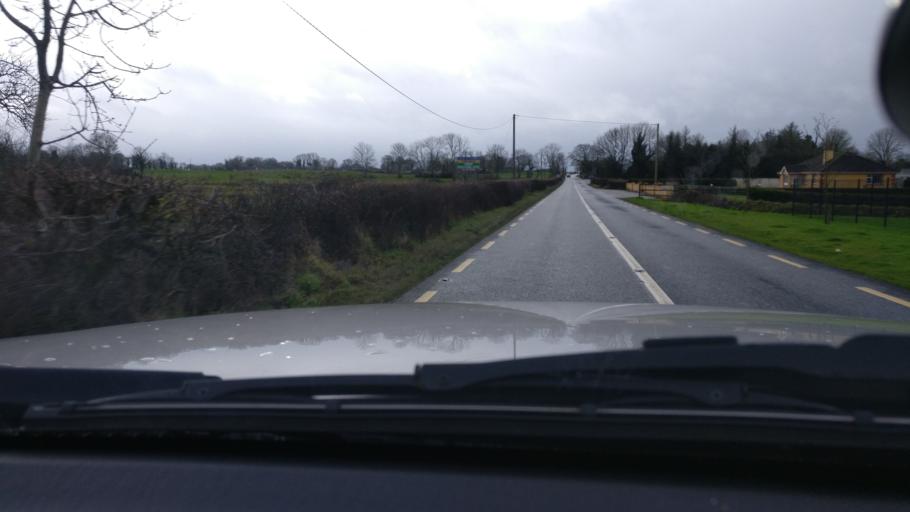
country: IE
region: Leinster
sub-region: An Longfort
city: Ballymahon
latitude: 53.5520
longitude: -7.7736
